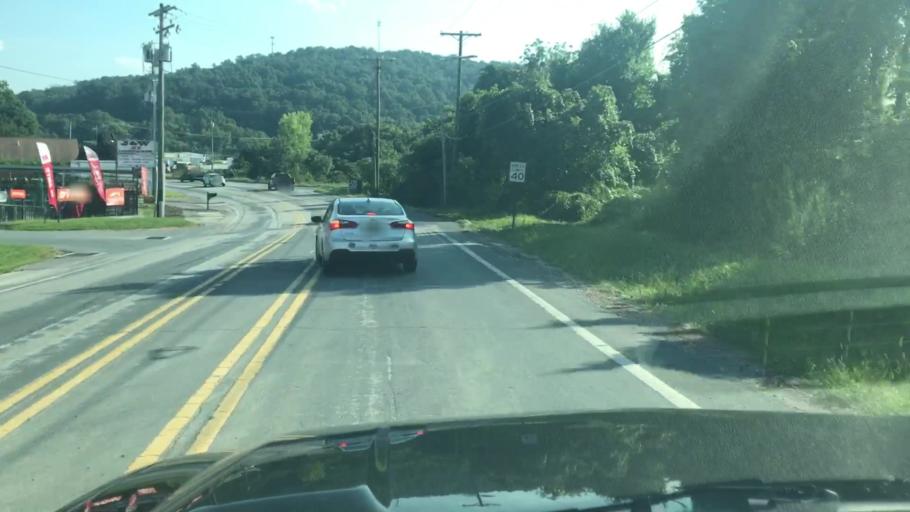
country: US
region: Pennsylvania
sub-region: York County
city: Valley Green
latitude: 40.1551
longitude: -76.8174
